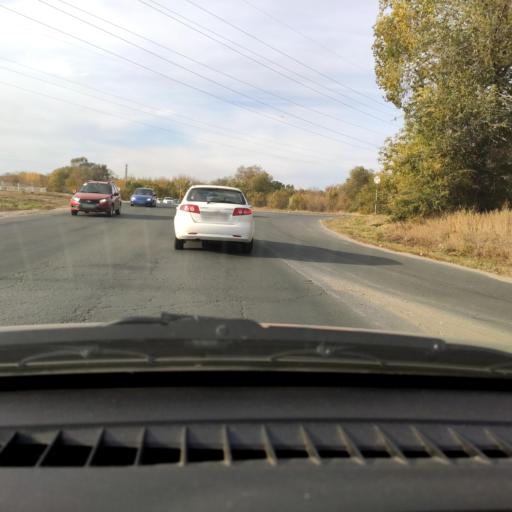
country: RU
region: Samara
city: Tol'yatti
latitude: 53.5657
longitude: 49.2896
